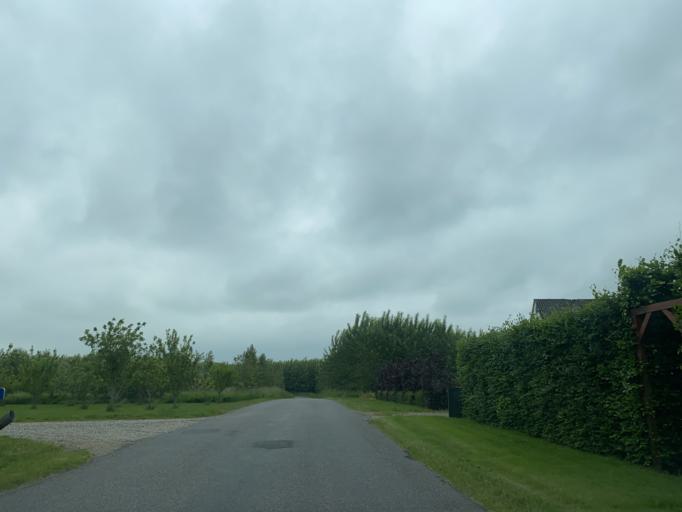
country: DK
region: Central Jutland
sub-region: Viborg Kommune
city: Bjerringbro
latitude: 56.3374
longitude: 9.6627
